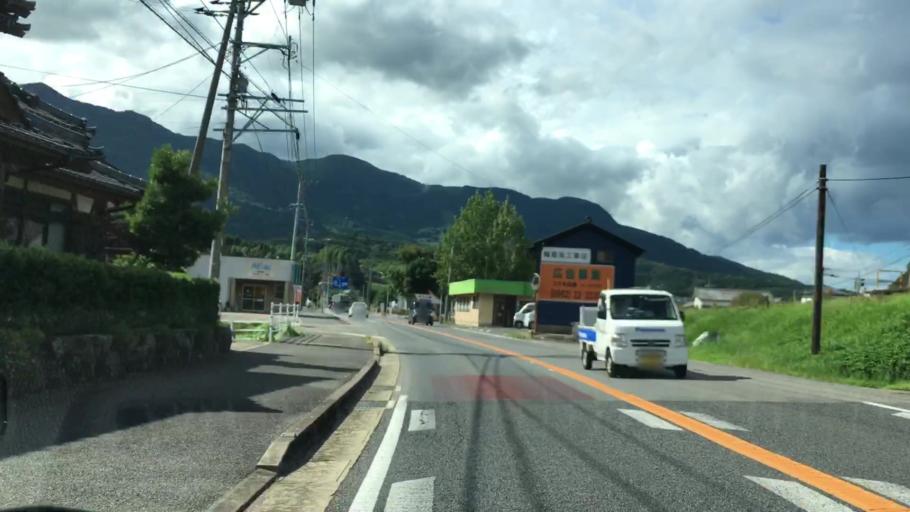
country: JP
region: Saga Prefecture
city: Imaricho-ko
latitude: 33.2219
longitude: 129.8497
